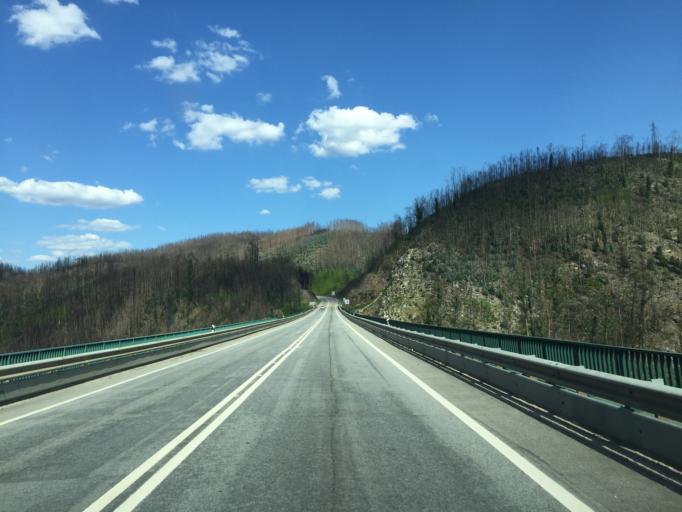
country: PT
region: Leiria
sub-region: Figueiro Dos Vinhos
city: Figueiro dos Vinhos
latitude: 39.9272
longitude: -8.3088
